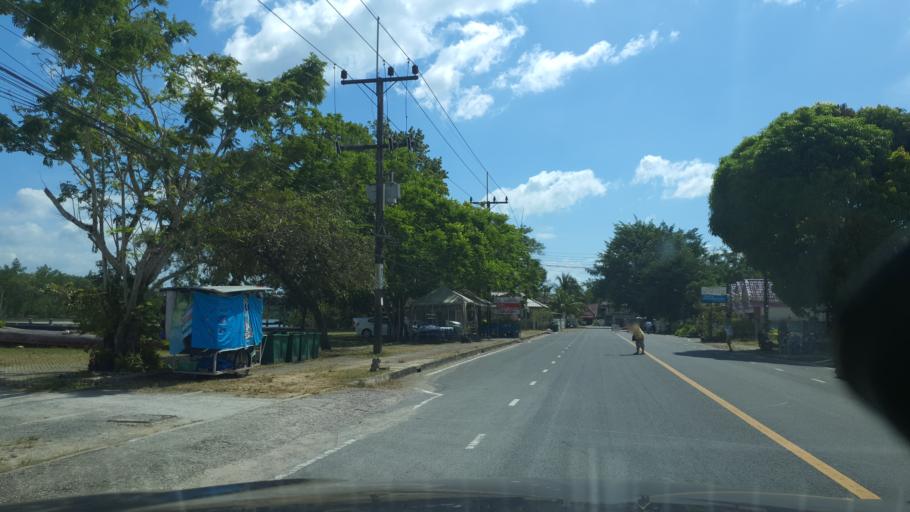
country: TH
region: Phangnga
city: Phang Nga
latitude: 8.3977
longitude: 98.5138
